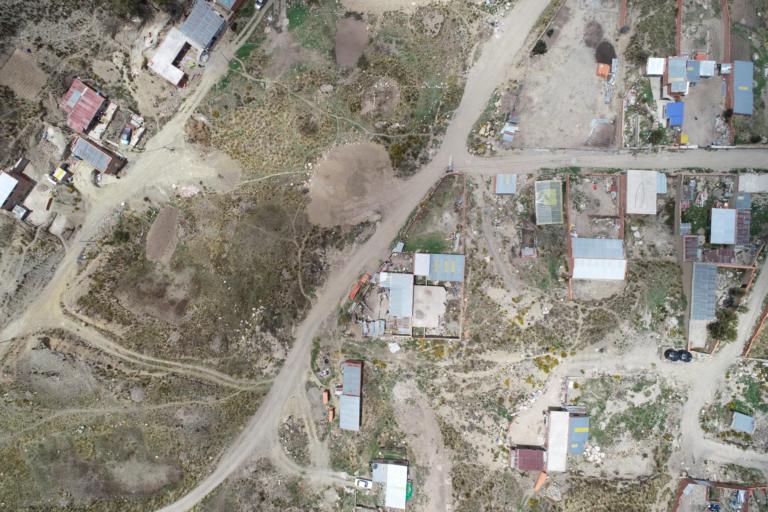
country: BO
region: La Paz
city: La Paz
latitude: -16.4427
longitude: -68.1422
